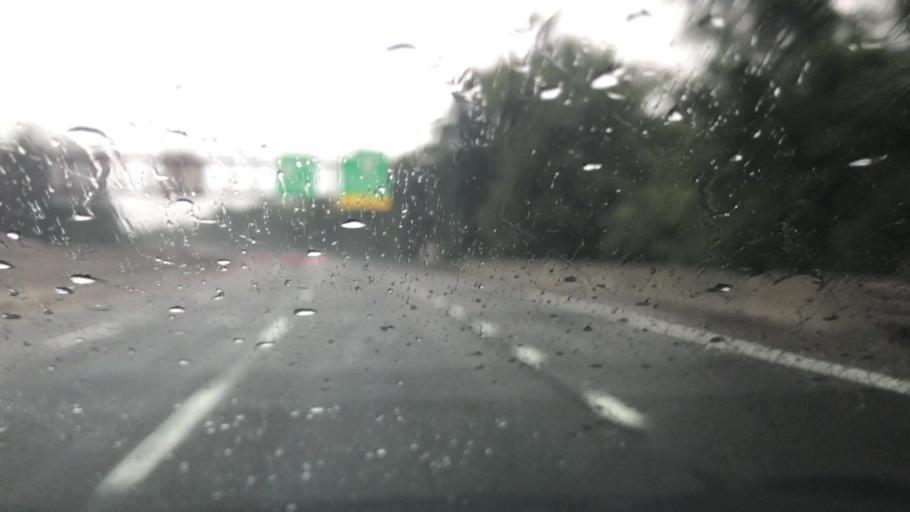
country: US
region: New Jersey
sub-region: Bergen County
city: Saddle Brook
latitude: 40.9098
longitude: -74.0936
